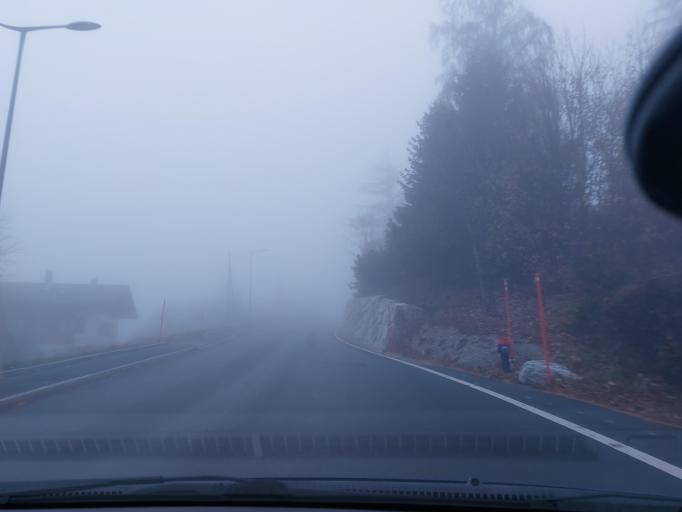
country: CH
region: Valais
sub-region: Sierre District
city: Lens
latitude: 46.2968
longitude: 7.4502
